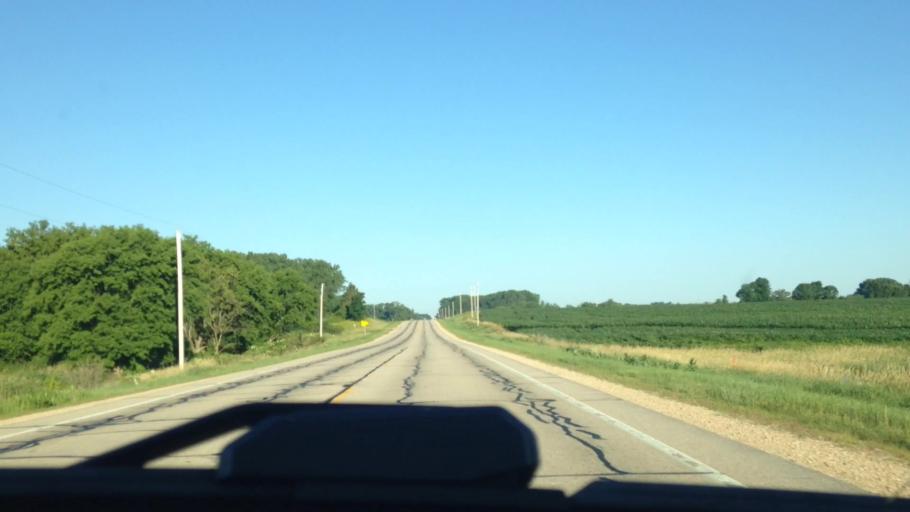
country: US
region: Wisconsin
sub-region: Columbia County
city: Fall River
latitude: 43.3409
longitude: -89.1132
